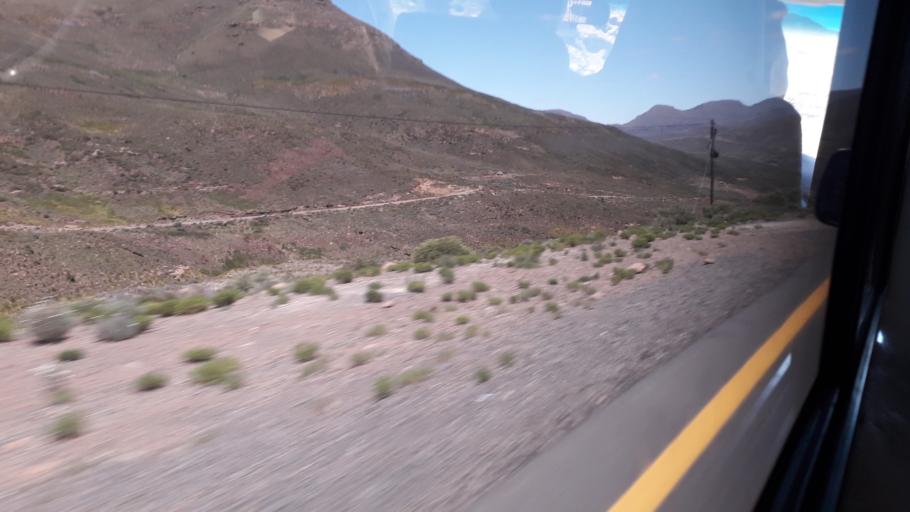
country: ZA
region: Orange Free State
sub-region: Thabo Mofutsanyana District Municipality
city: Phuthaditjhaba
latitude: -28.7724
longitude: 28.6684
